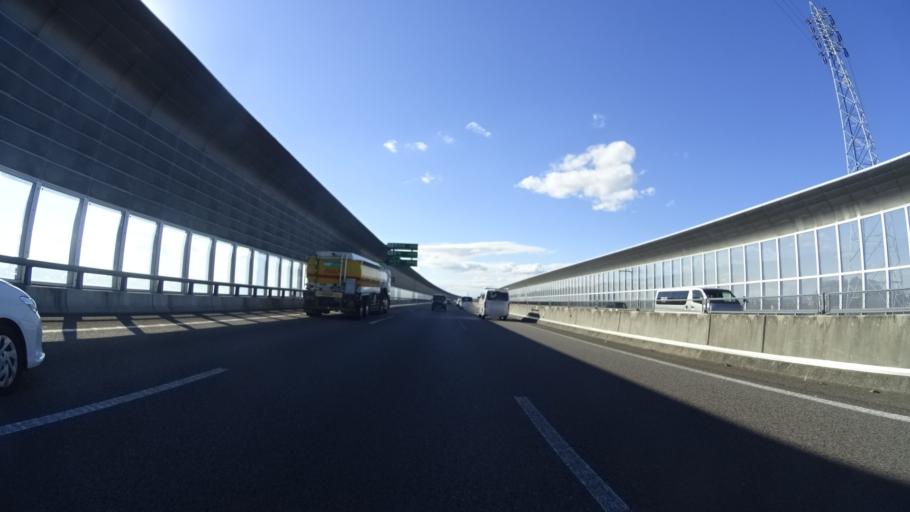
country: JP
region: Aichi
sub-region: Toyota-shi
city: Toyota
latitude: 35.0140
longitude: 137.1280
